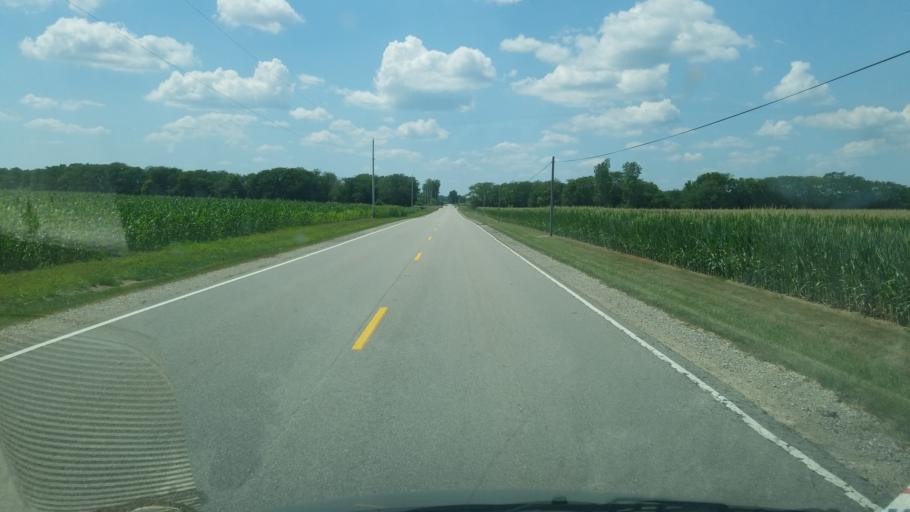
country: US
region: Ohio
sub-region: Champaign County
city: North Lewisburg
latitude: 40.1492
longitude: -83.4802
